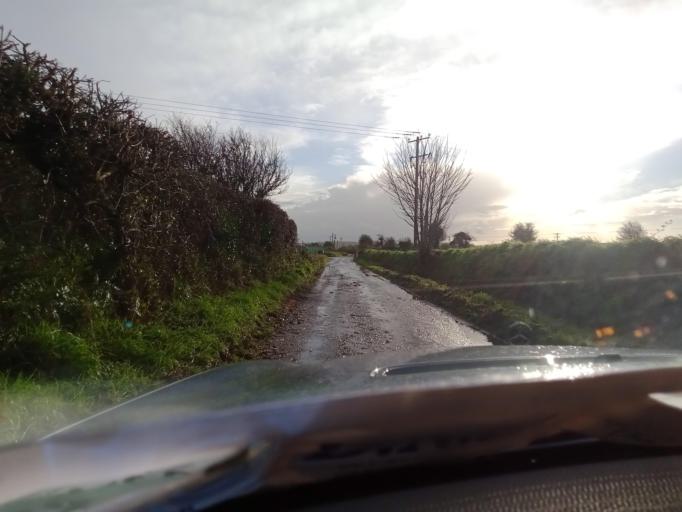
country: IE
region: Leinster
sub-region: Kilkenny
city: Mooncoin
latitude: 52.2794
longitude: -7.1919
